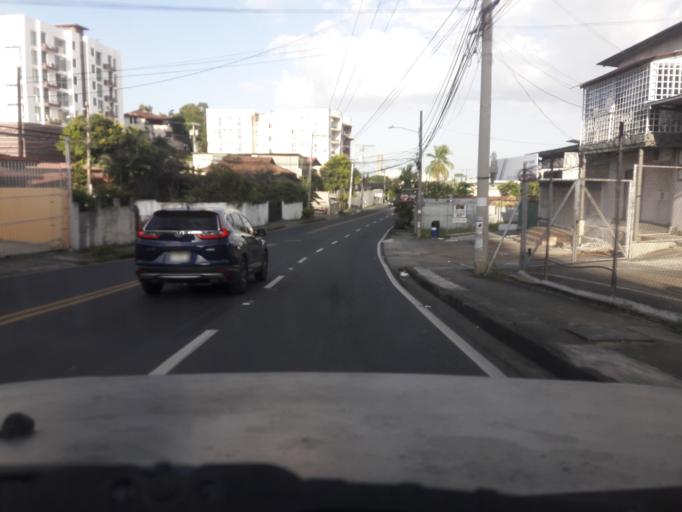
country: PA
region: Panama
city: Panama
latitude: 9.0152
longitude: -79.5063
